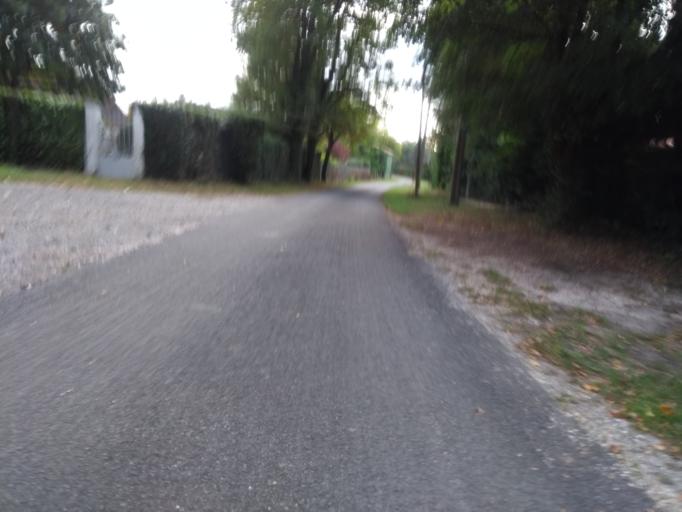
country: FR
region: Aquitaine
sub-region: Departement de la Gironde
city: Gradignan
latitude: 44.7838
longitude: -0.6218
